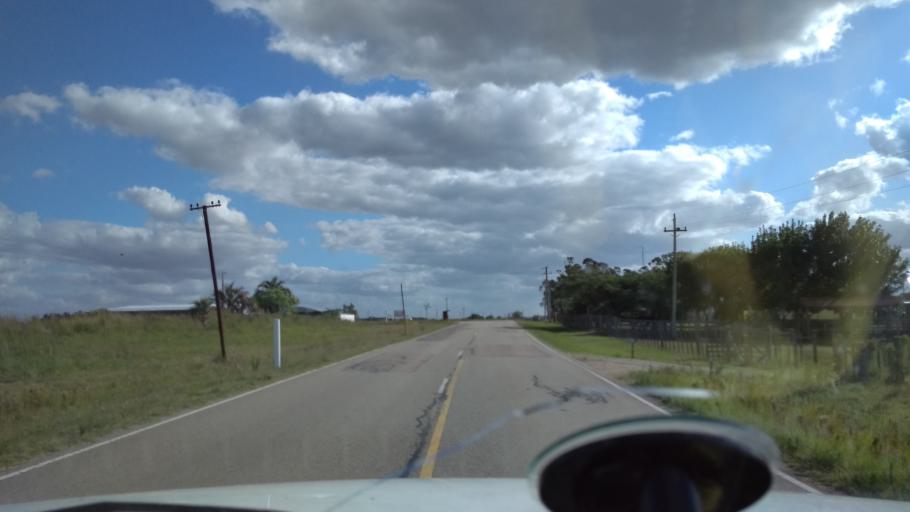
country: UY
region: Florida
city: Casupa
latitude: -34.1486
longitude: -55.6814
